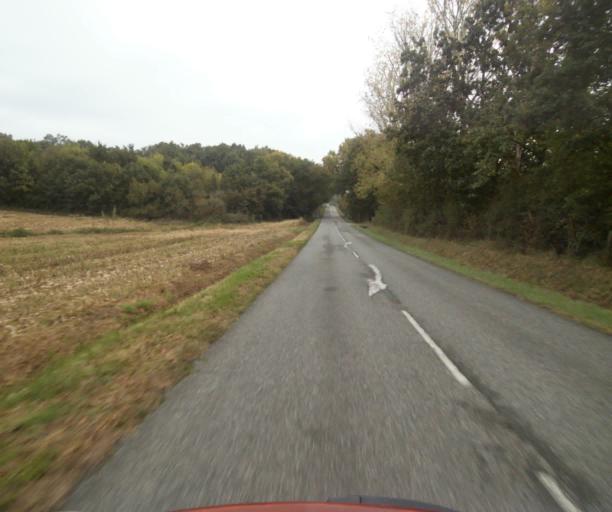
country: FR
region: Midi-Pyrenees
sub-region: Departement du Tarn-et-Garonne
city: Verdun-sur-Garonne
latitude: 43.8417
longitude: 1.1920
